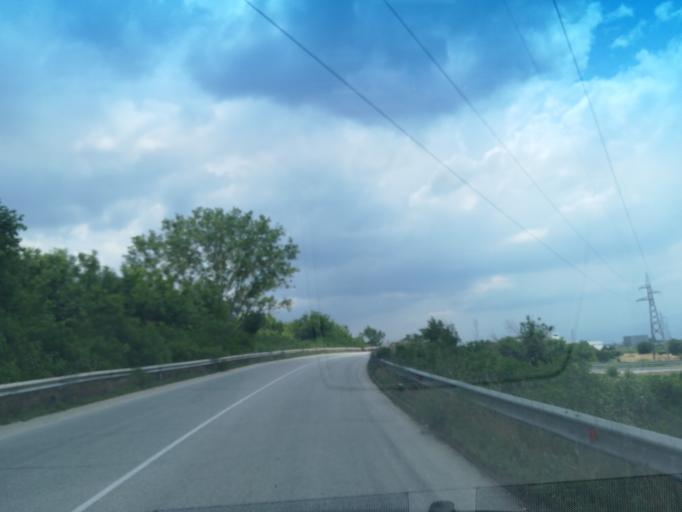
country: BG
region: Plovdiv
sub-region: Obshtina Plovdiv
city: Plovdiv
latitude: 42.2032
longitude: 24.6676
